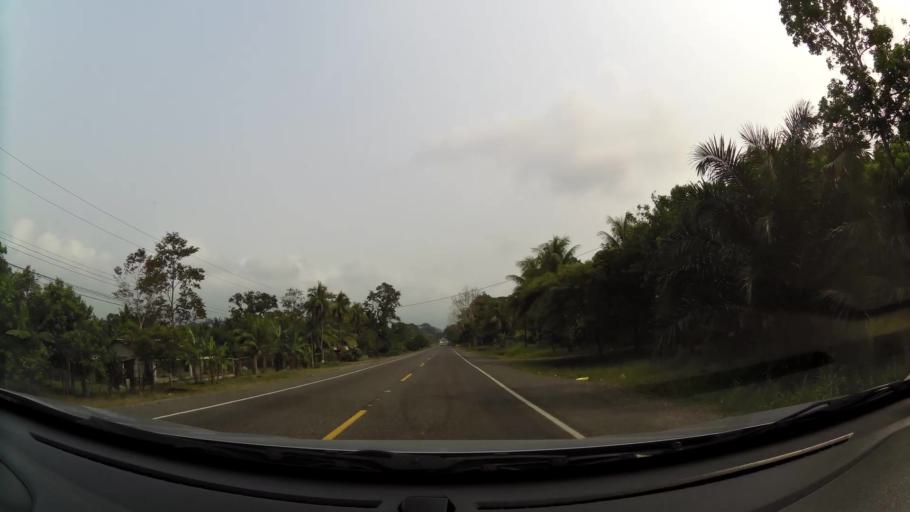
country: HN
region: Atlantida
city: Mezapa
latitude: 15.5996
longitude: -87.6097
